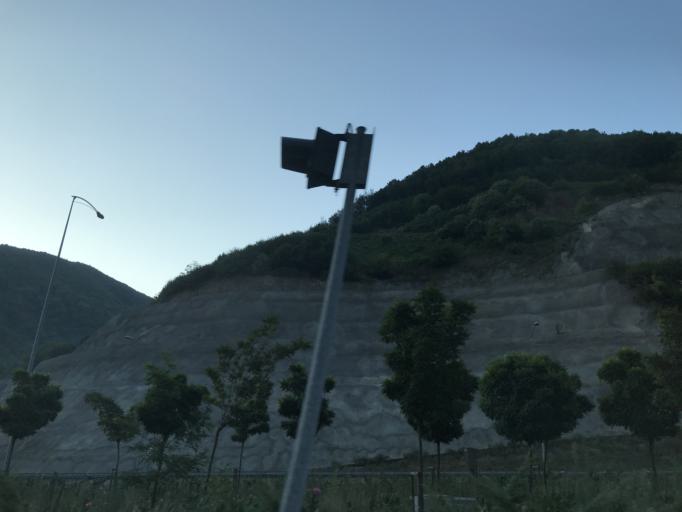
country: TR
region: Bursa
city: Yenikoy
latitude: 40.5838
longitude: 29.3624
